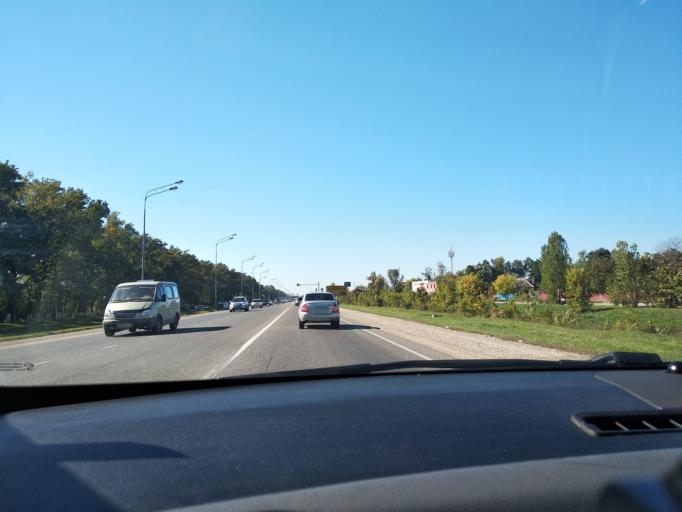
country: RU
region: Krasnodarskiy
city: Novotitarovskaya
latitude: 45.1410
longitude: 39.0396
